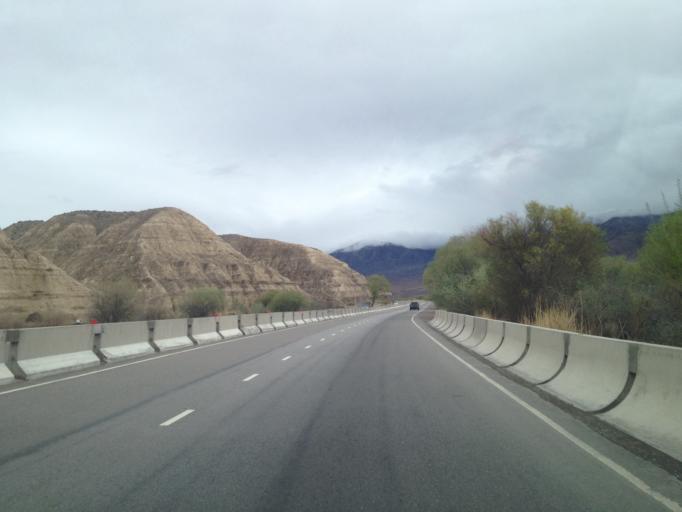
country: KG
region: Naryn
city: Kochkor
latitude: 42.4917
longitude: 75.8538
